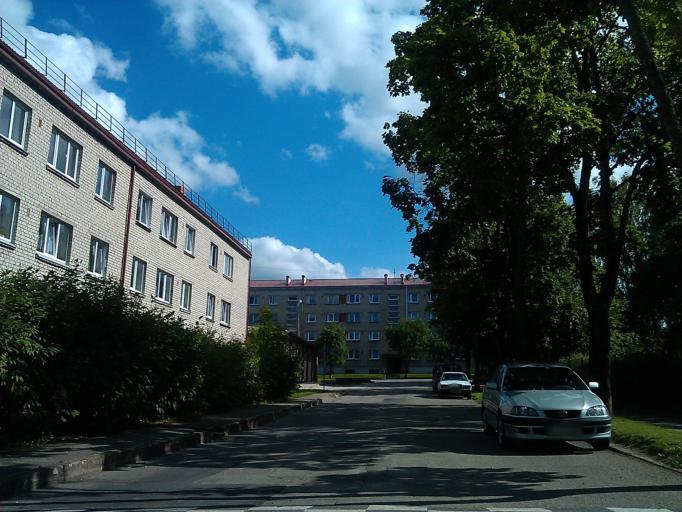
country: LV
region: Cesu Rajons
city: Cesis
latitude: 57.3049
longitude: 25.2690
